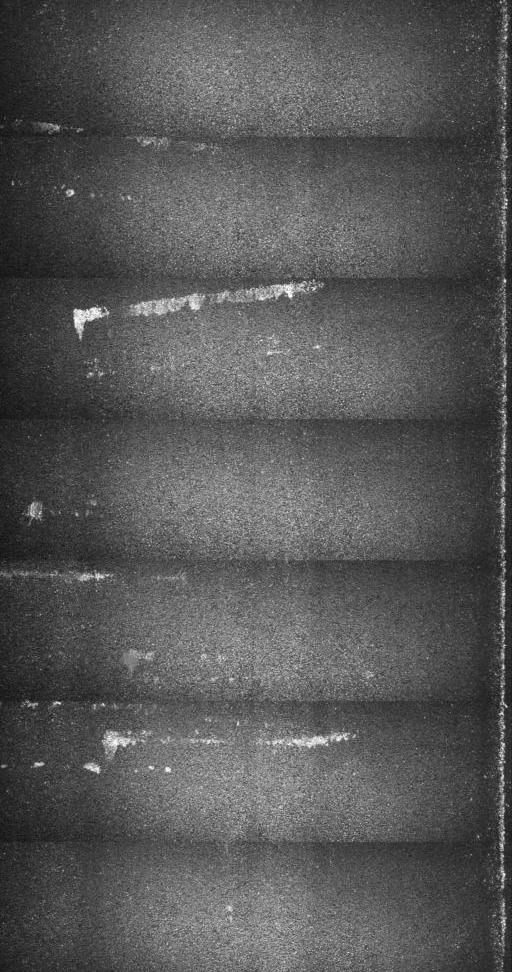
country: US
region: Vermont
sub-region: Franklin County
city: Richford
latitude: 44.8300
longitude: -72.6092
